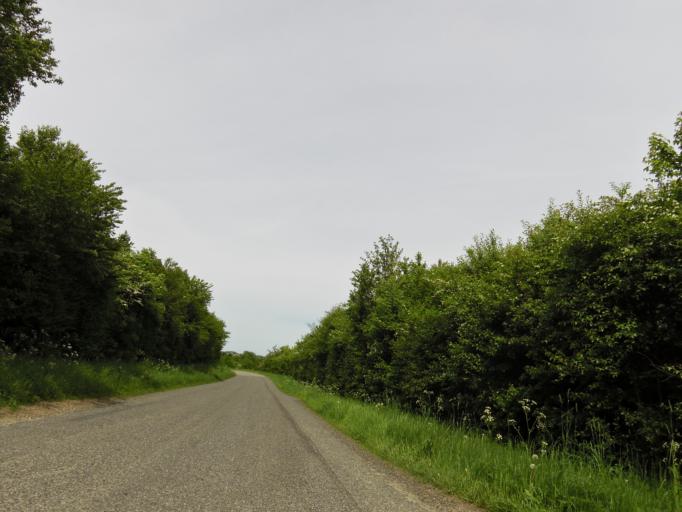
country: DK
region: Central Jutland
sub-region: Holstebro Kommune
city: Vinderup
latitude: 56.5461
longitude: 8.8873
